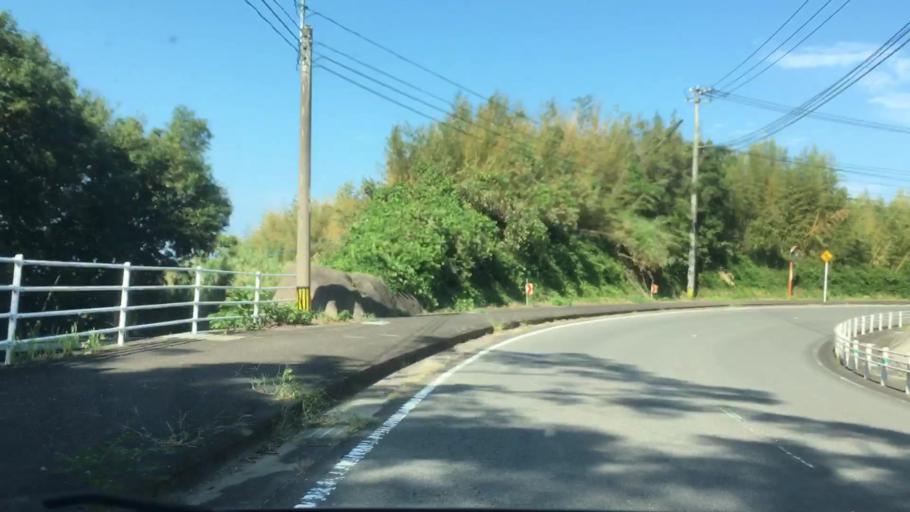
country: JP
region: Nagasaki
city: Sasebo
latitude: 33.0118
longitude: 129.6547
